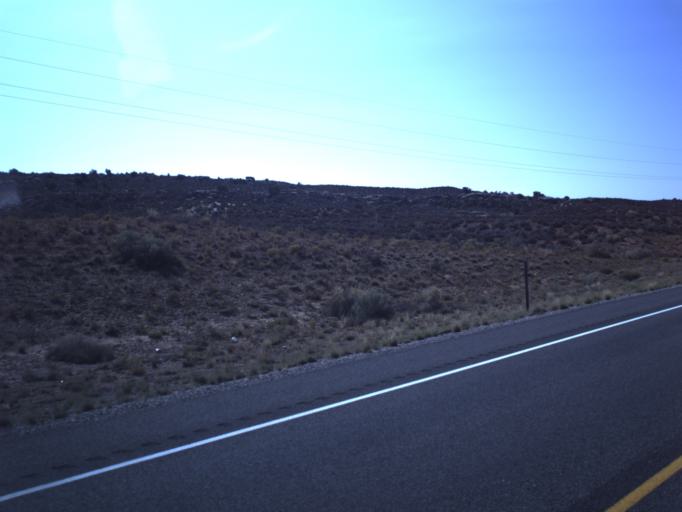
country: US
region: Utah
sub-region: San Juan County
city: Blanding
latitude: 37.3716
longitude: -109.5064
